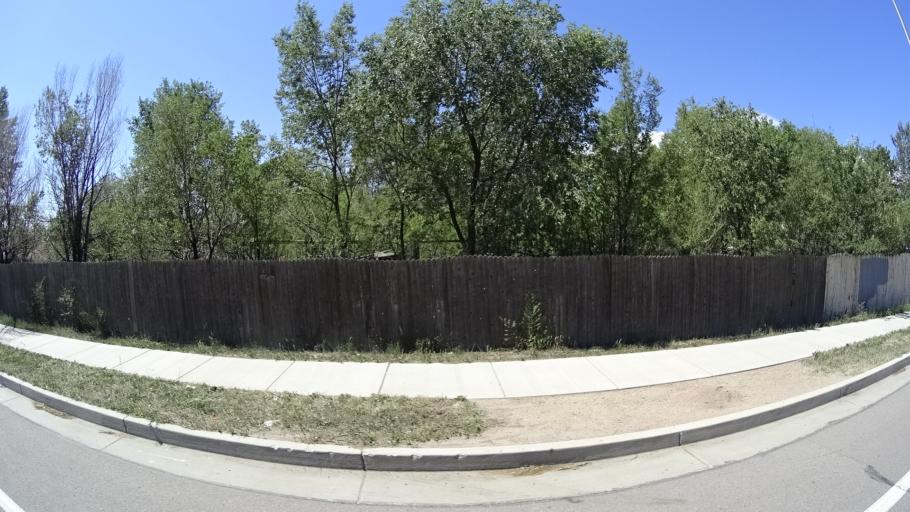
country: US
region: Colorado
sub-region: El Paso County
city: Stratmoor
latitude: 38.7933
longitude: -104.7667
